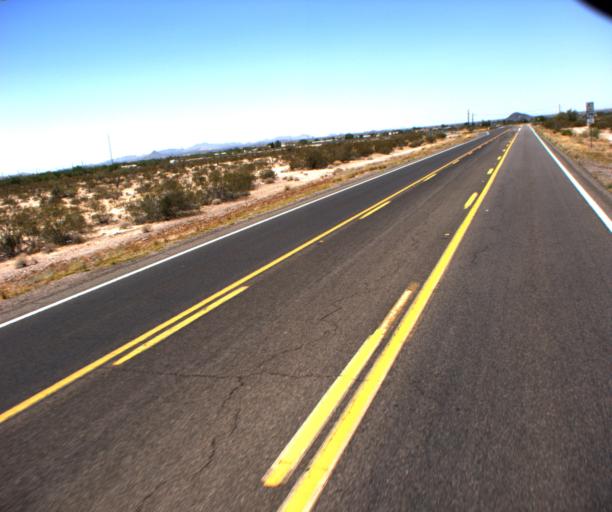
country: US
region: Arizona
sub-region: Pinal County
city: Florence
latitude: 33.0067
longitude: -111.3745
